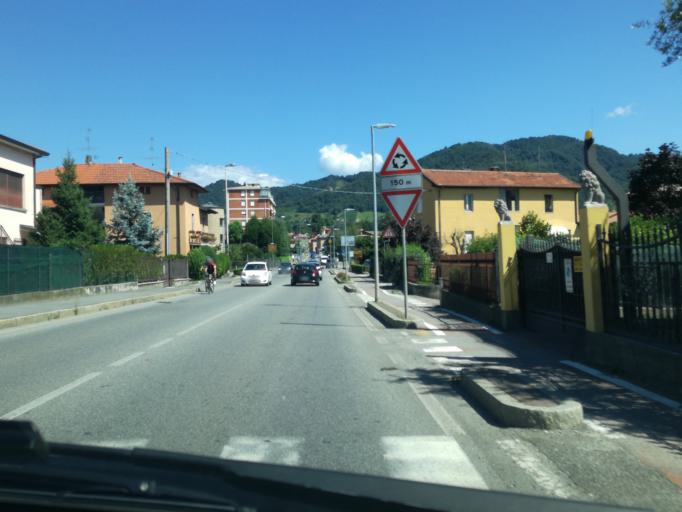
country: IT
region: Lombardy
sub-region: Provincia di Bergamo
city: Carvico
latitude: 45.6992
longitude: 9.4801
